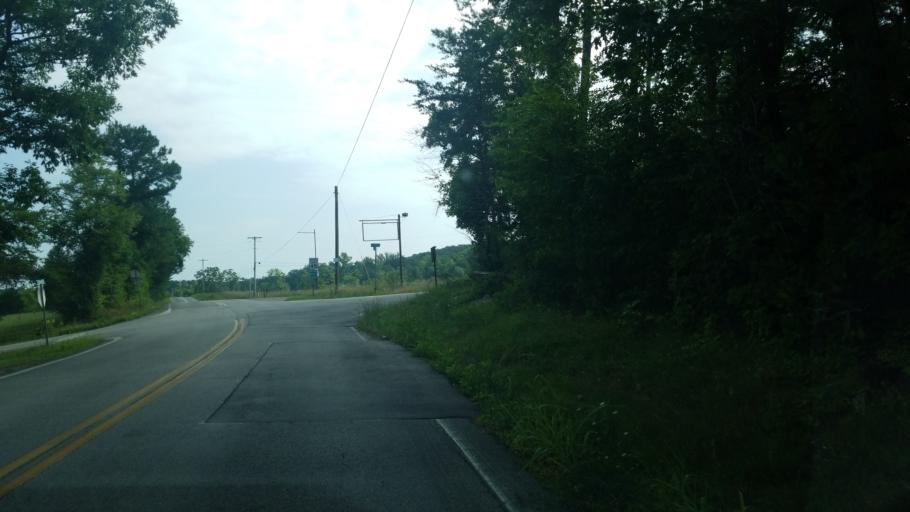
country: US
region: Tennessee
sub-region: Hamilton County
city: Apison
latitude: 35.0346
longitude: -84.9942
